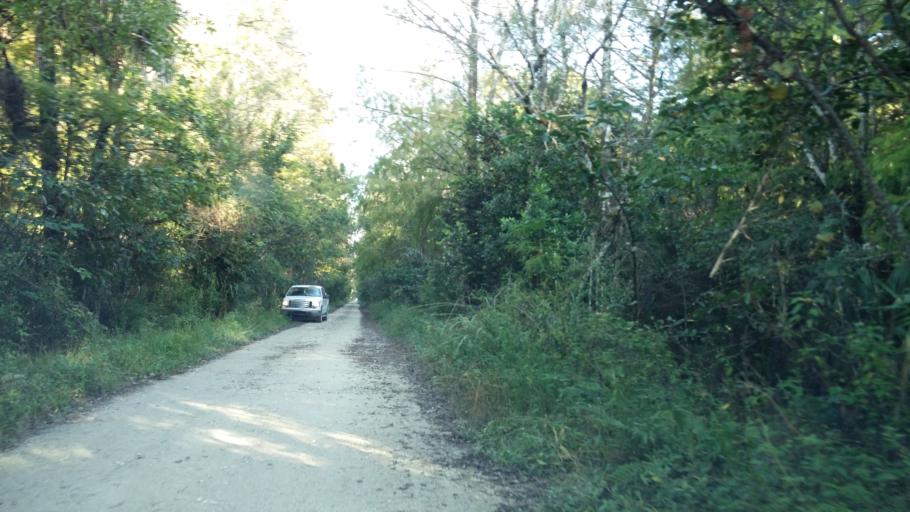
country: US
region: Florida
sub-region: Collier County
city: Lely Resort
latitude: 25.9800
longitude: -81.4001
